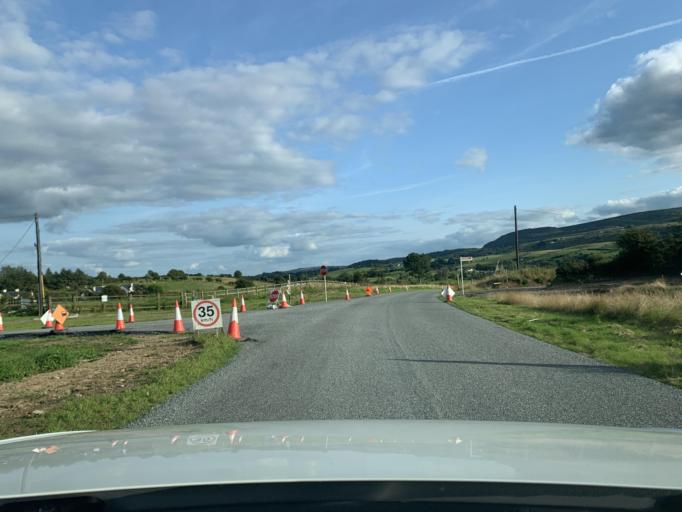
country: IE
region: Connaught
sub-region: Roscommon
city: Boyle
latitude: 54.0829
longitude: -8.3707
